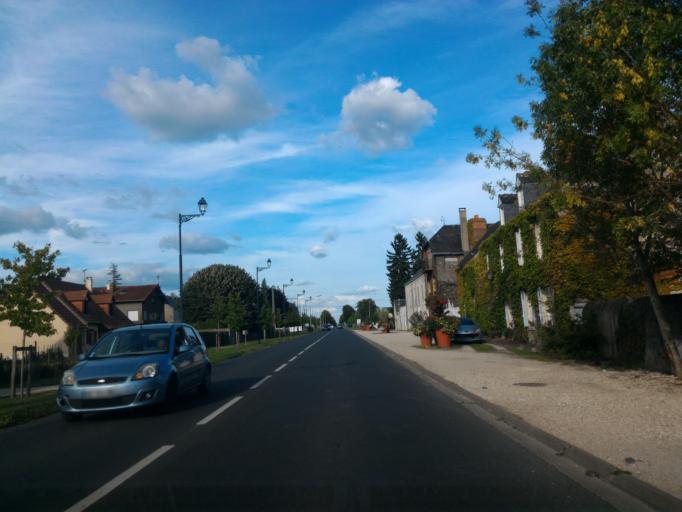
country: FR
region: Centre
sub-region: Departement du Loir-et-Cher
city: Saint-Dye-sur-Loire
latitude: 47.6565
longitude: 1.4920
